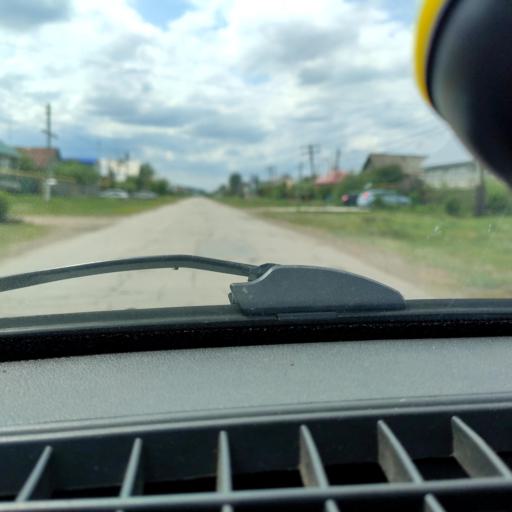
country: RU
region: Samara
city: Povolzhskiy
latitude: 53.6423
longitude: 49.6891
